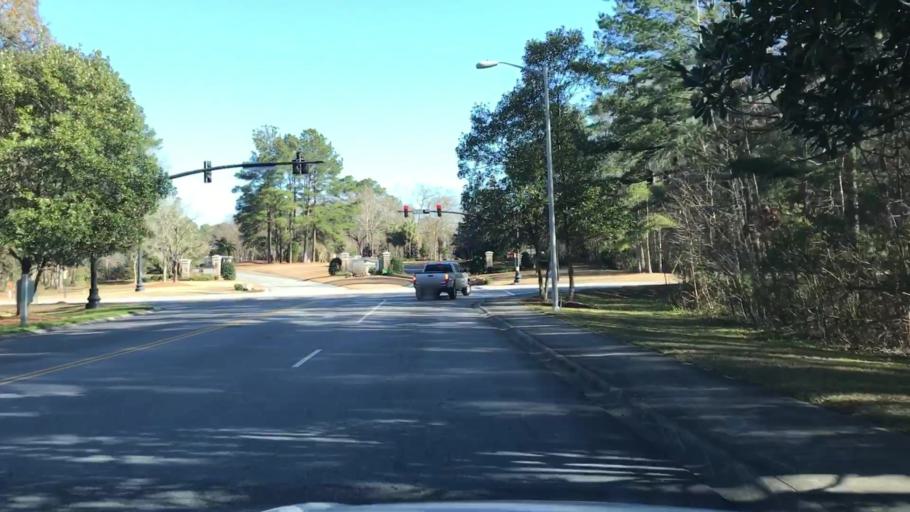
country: US
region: South Carolina
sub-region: Berkeley County
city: Ladson
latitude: 32.9257
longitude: -80.1160
